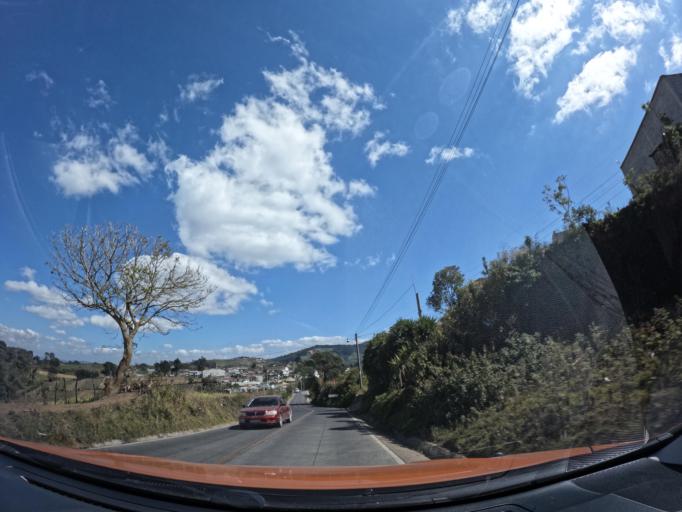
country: GT
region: Chimaltenango
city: Patzun
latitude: 14.6479
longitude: -91.0422
